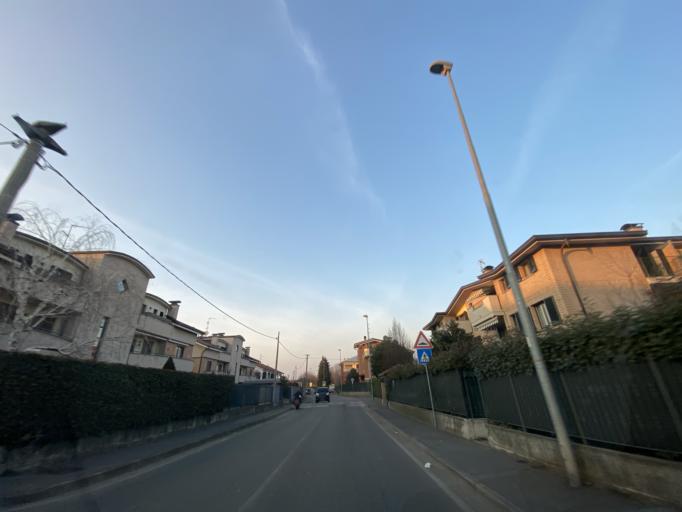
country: IT
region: Lombardy
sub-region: Citta metropolitana di Milano
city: Cesate
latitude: 45.5950
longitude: 9.0663
